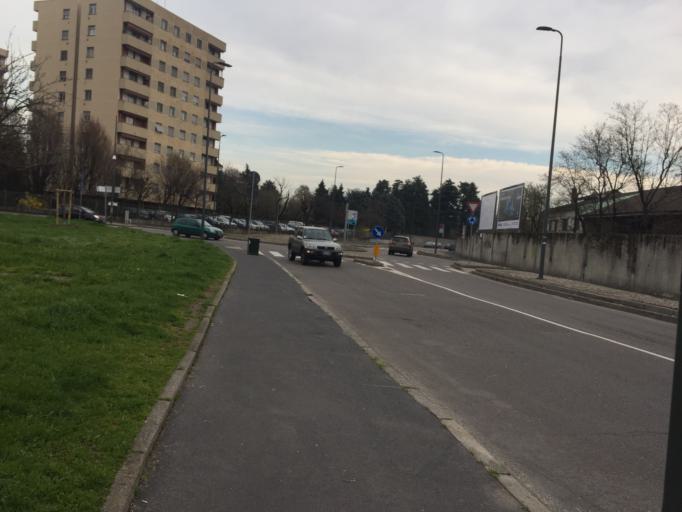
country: IT
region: Lombardy
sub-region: Citta metropolitana di Milano
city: Pero
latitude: 45.4883
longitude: 9.1178
